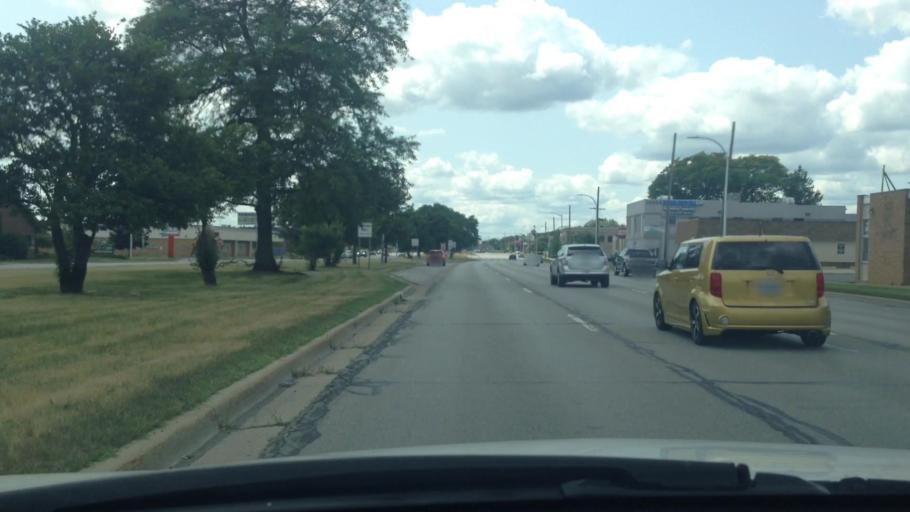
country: US
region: Michigan
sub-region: Wayne County
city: Inkster
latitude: 42.2984
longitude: -83.2794
